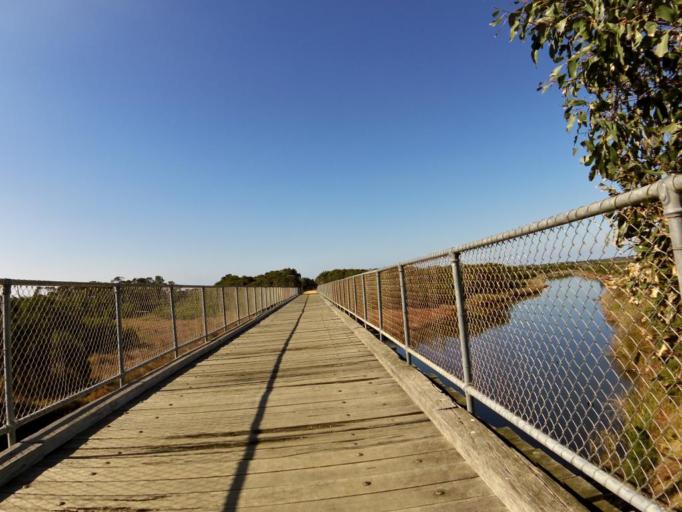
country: AU
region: Victoria
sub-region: Bass Coast
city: North Wonthaggi
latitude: -38.5742
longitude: 145.5468
